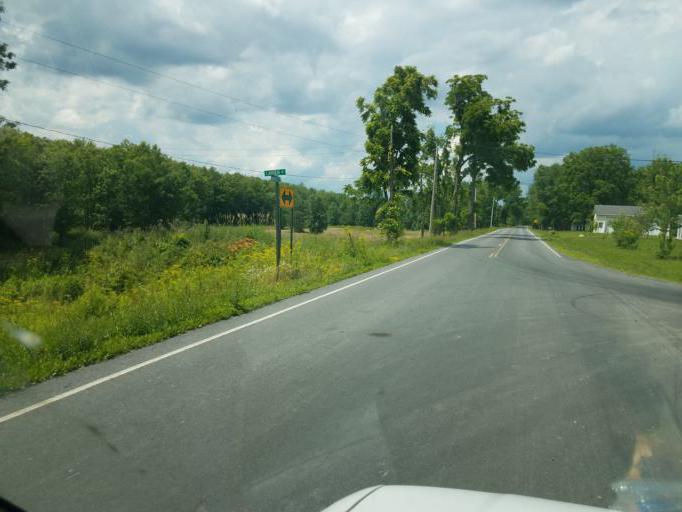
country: US
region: New York
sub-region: Seneca County
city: Waterloo
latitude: 42.9887
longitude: -76.8693
